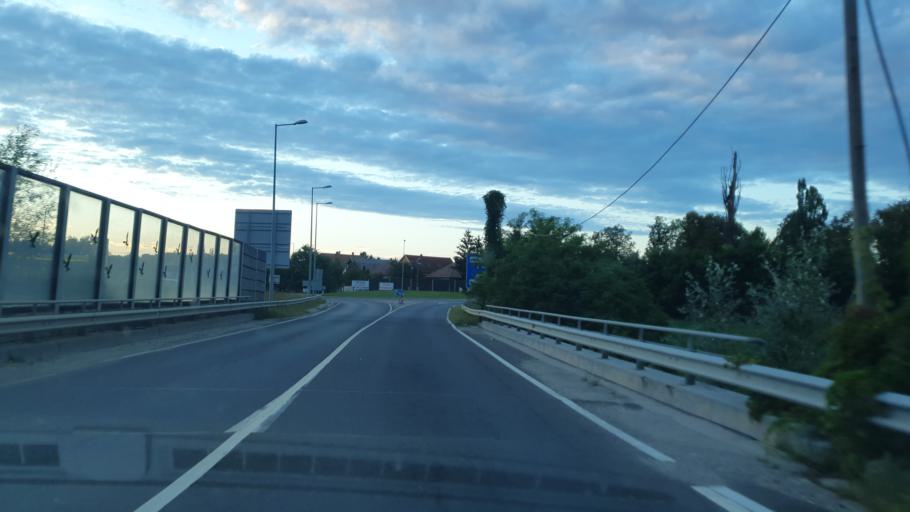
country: HU
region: Pest
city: Bag
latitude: 47.6364
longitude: 19.4729
